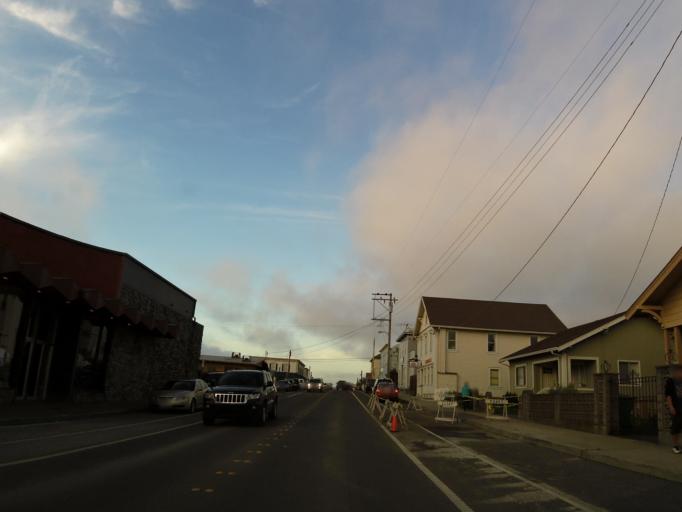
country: US
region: California
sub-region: Mendocino County
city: Fort Bragg
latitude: 39.4408
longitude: -123.8046
